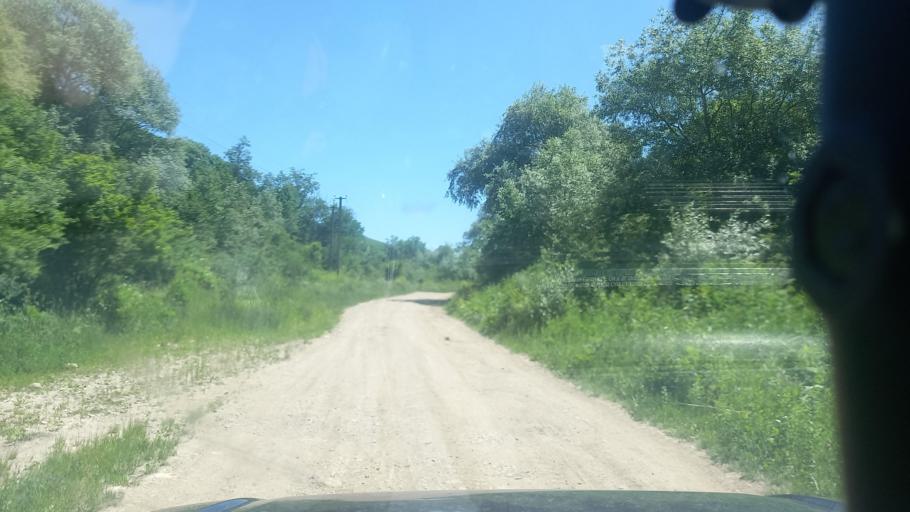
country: RU
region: Karachayevo-Cherkesiya
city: Pregradnaya
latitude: 44.1148
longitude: 41.1012
